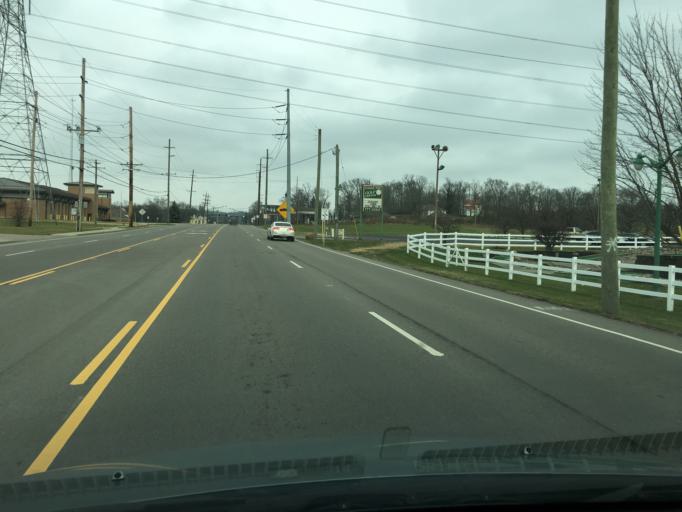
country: US
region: Ohio
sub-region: Butler County
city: Beckett Ridge
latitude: 39.3222
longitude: -84.4108
